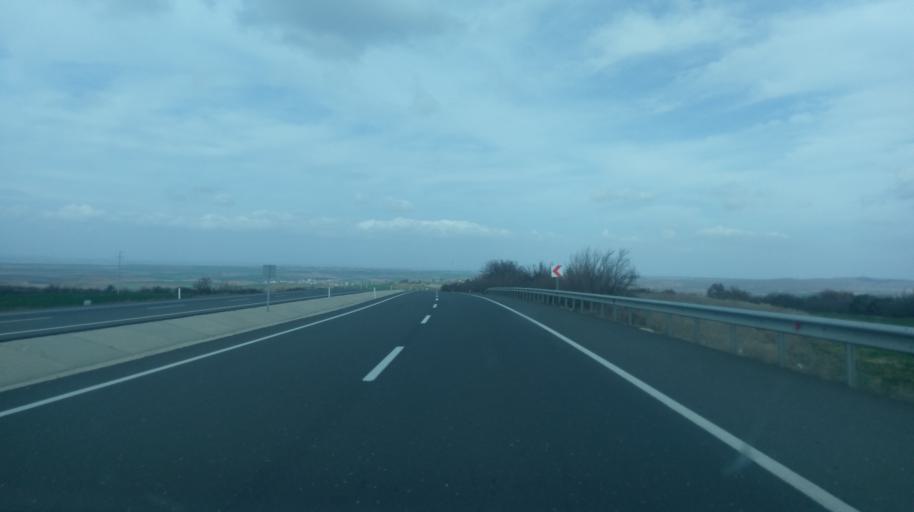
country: TR
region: Edirne
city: Hamidiye
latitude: 41.0817
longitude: 26.6400
